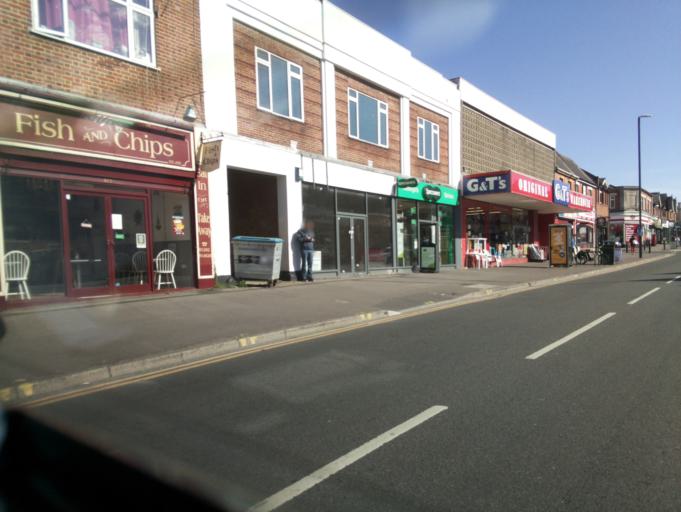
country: GB
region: England
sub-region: Bournemouth
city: Bournemouth
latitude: 50.7429
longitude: -1.8788
